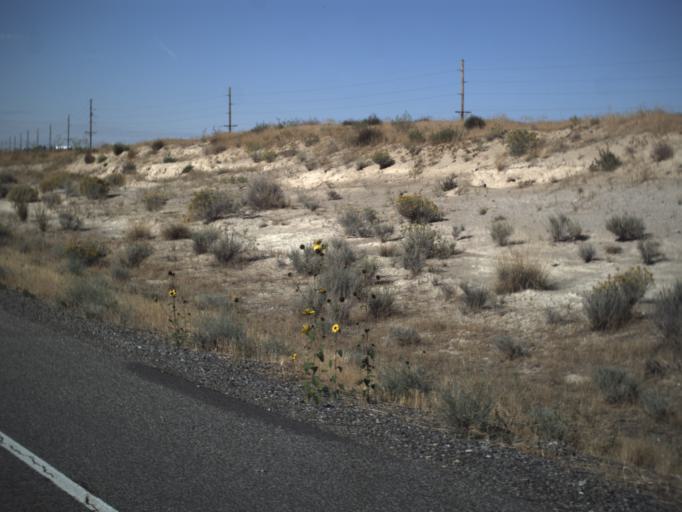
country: US
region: Utah
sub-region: Tooele County
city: Grantsville
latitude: 40.7676
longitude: -112.9877
